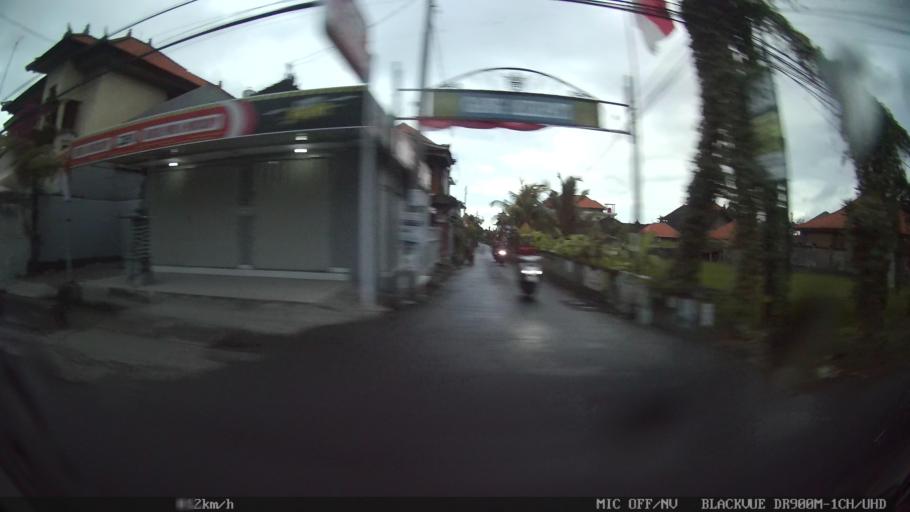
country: ID
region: Bali
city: Banjar Kertajiwa
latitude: -8.6269
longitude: 115.2655
